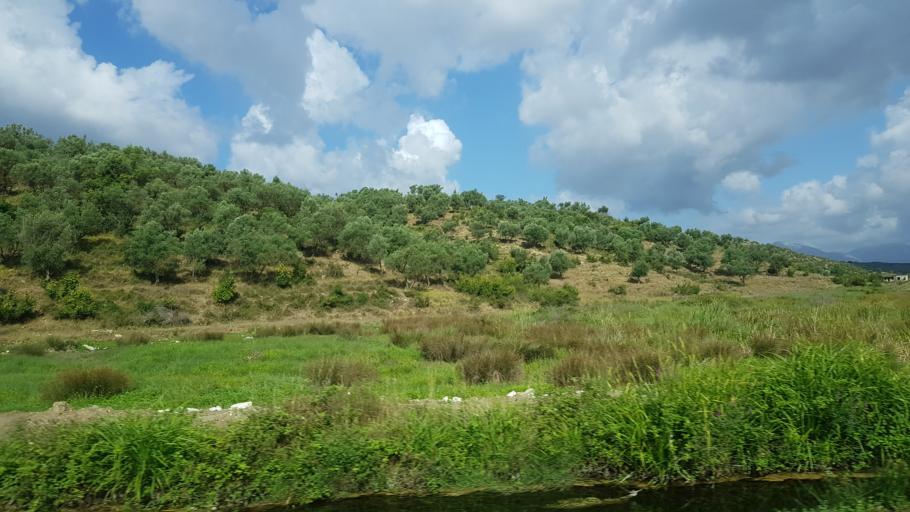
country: AL
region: Vlore
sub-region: Rrethi i Delvines
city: Mesopotam
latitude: 39.9045
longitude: 20.0849
